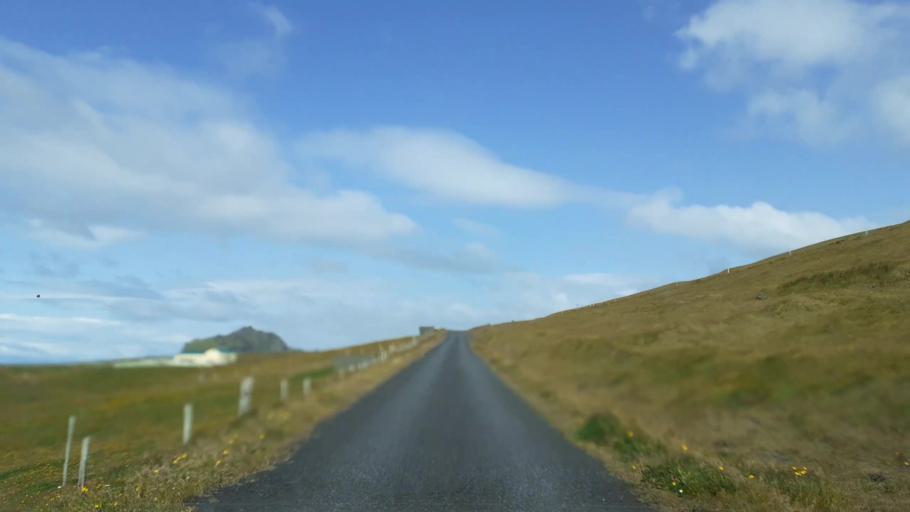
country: IS
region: South
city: Vestmannaeyjar
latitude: 63.4150
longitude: -20.2808
